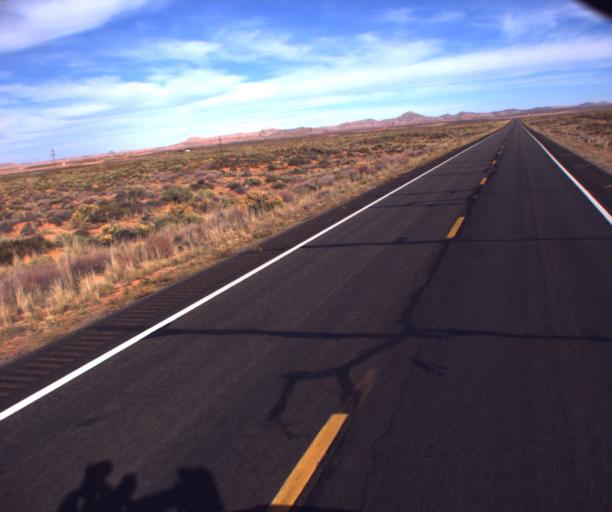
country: US
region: Arizona
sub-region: Apache County
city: Many Farms
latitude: 36.9402
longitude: -109.6731
